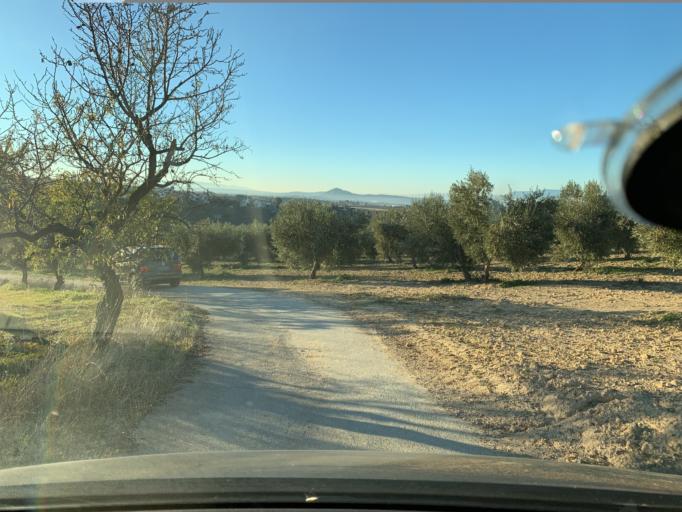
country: ES
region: Andalusia
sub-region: Provincia de Granada
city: Dilar
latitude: 37.0756
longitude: -3.5913
